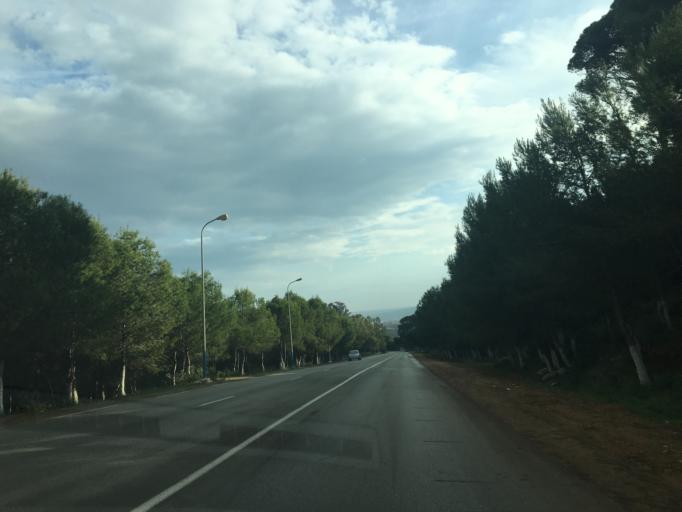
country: DZ
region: Tipaza
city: Tipasa
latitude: 36.5892
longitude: 2.4805
